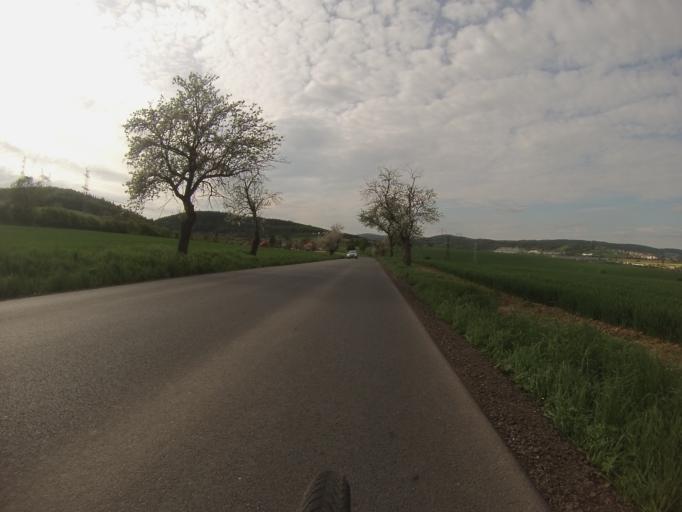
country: CZ
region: South Moravian
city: Cebin
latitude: 49.3089
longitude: 16.4594
